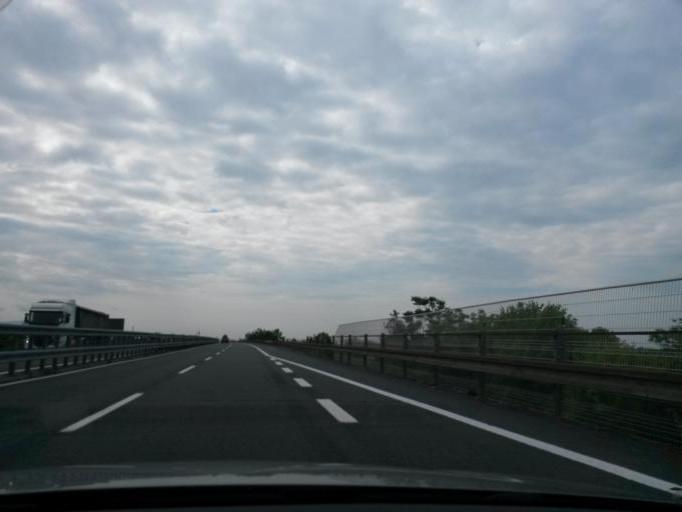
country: IT
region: Tuscany
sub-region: Provincia di Lucca
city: Pietrasanta
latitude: 43.9262
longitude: 10.2252
